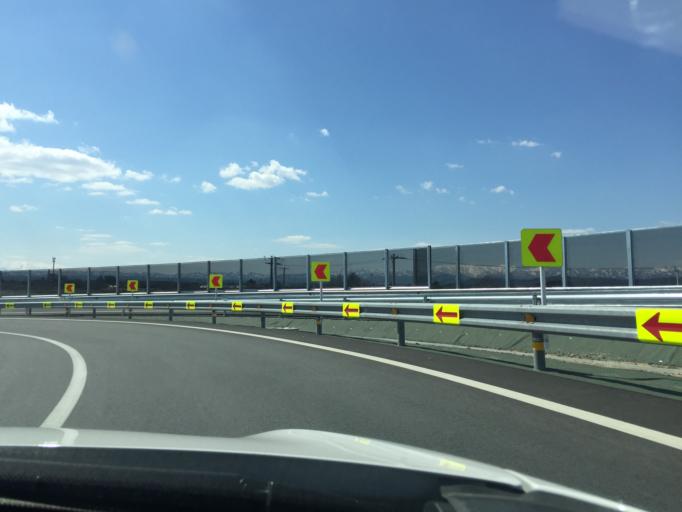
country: JP
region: Yamagata
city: Takahata
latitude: 38.0262
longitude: 140.1641
